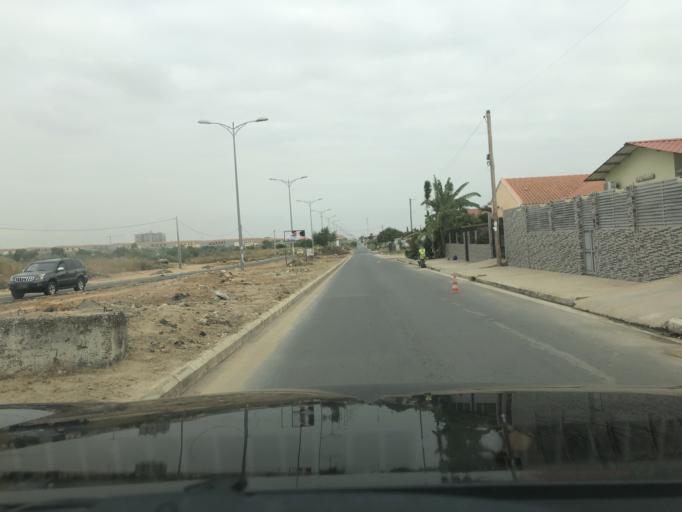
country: AO
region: Luanda
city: Luanda
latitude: -8.9455
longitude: 13.2535
